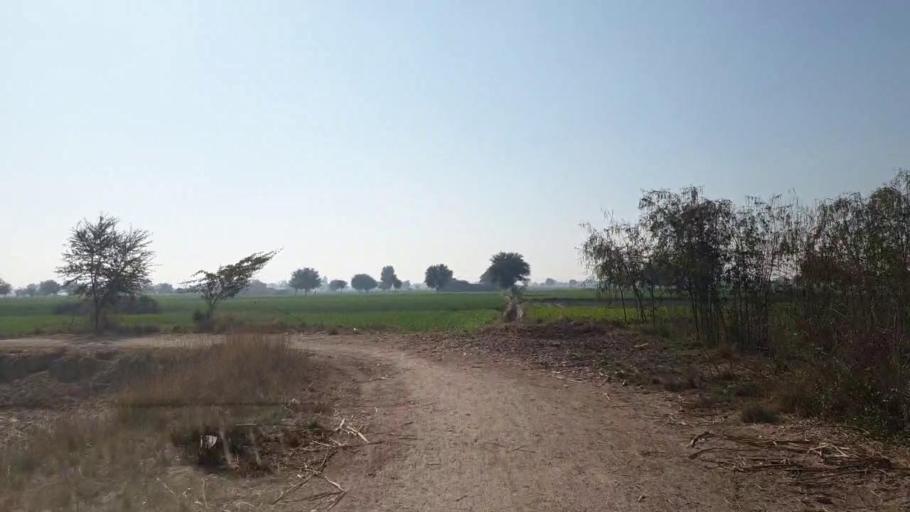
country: PK
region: Sindh
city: Nawabshah
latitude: 26.0809
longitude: 68.4789
